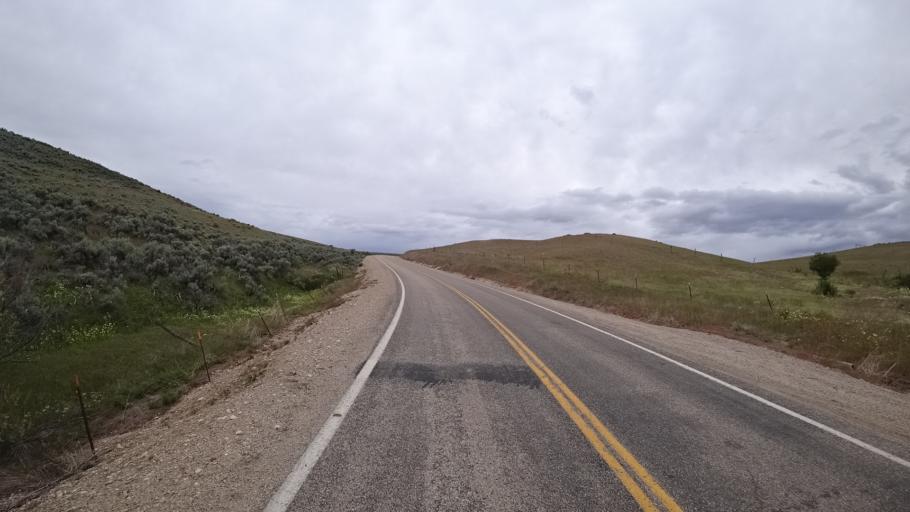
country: US
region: Idaho
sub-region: Ada County
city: Boise
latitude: 43.4871
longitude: -116.0054
